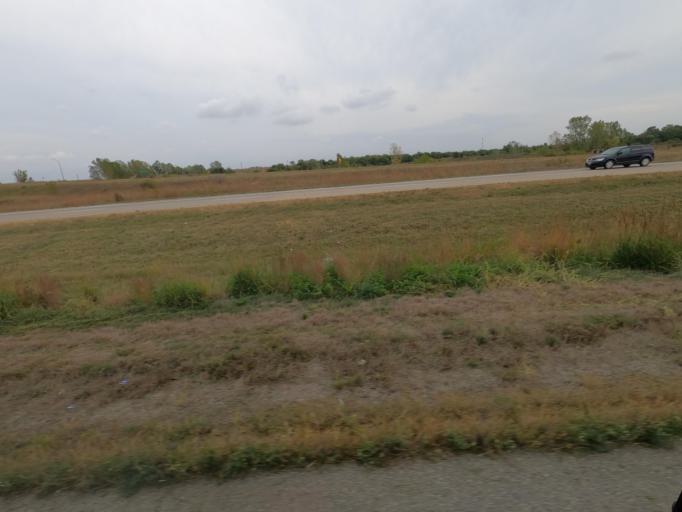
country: US
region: Iowa
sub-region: Jasper County
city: Monroe
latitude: 41.5421
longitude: -93.1304
